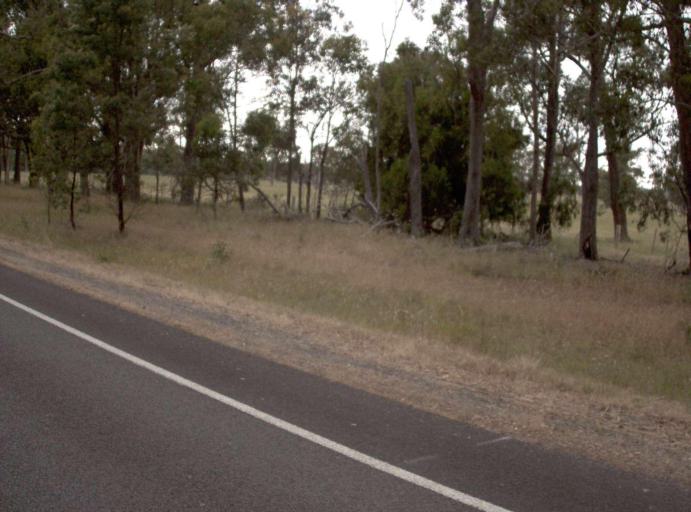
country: AU
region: Victoria
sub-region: Wellington
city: Sale
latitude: -38.4424
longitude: 146.9454
